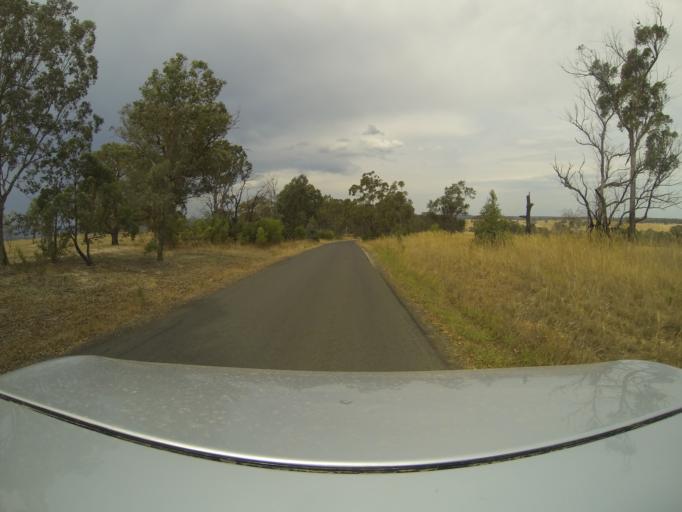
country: AU
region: Victoria
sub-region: Wellington
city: Heyfield
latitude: -37.9069
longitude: 146.7138
